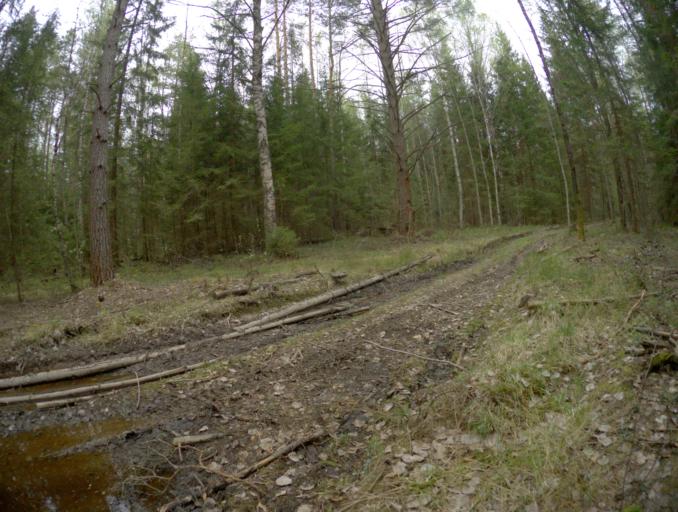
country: RU
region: Vladimir
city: Golovino
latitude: 55.9093
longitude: 40.4571
